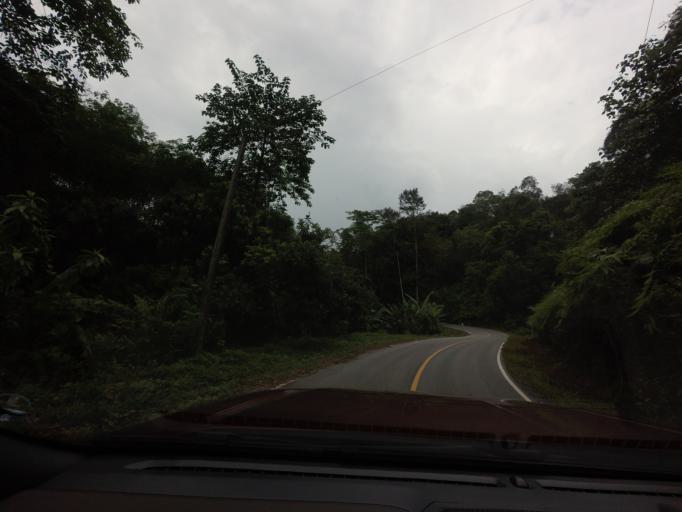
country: TH
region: Narathiwat
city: Sukhirin
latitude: 5.9790
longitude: 101.6816
